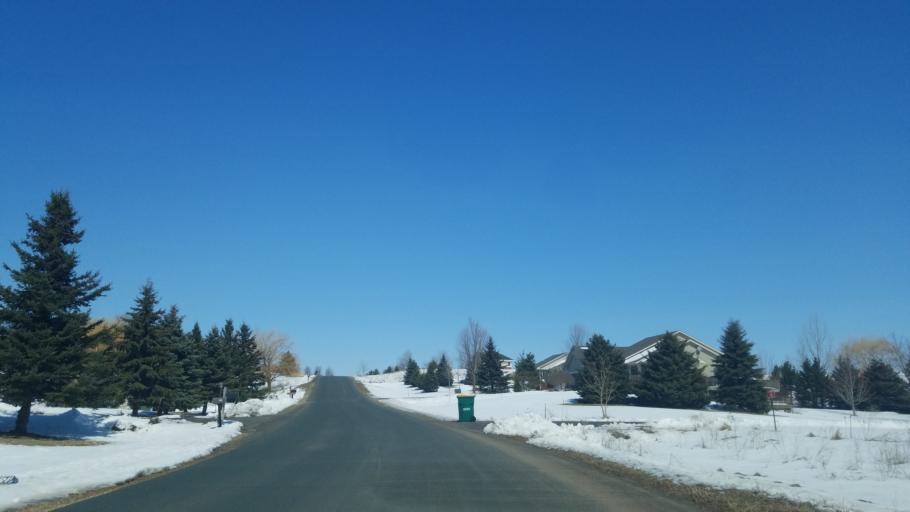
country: US
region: Wisconsin
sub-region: Saint Croix County
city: North Hudson
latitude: 44.9979
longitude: -92.6585
